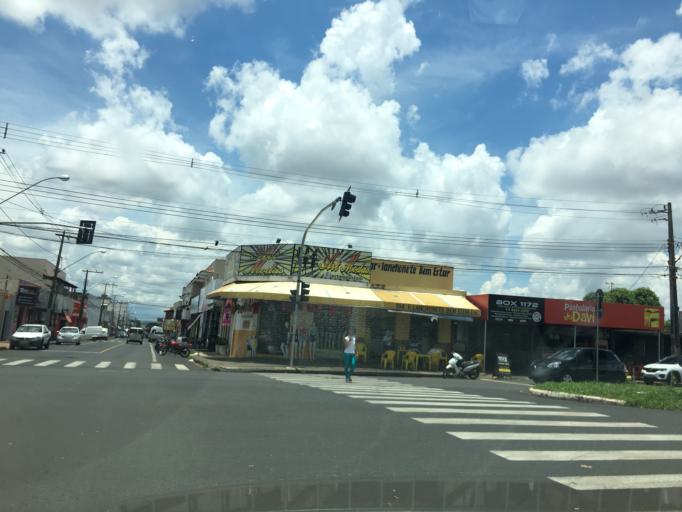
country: BR
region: Minas Gerais
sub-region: Uberlandia
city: Uberlandia
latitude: -18.9372
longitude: -48.3158
